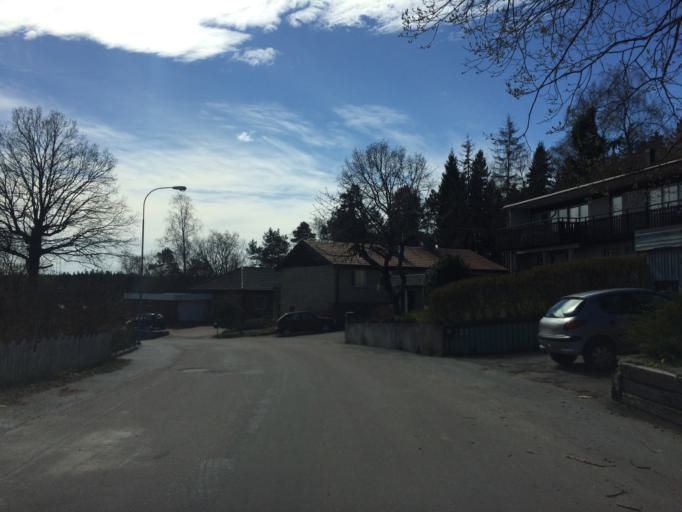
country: SE
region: Stockholm
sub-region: Sollentuna Kommun
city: Sollentuna
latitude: 59.4515
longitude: 17.9133
